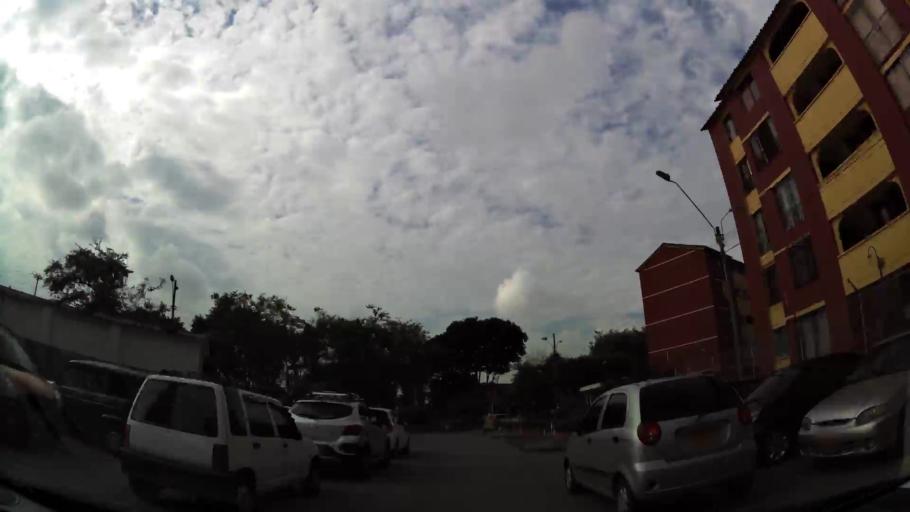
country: CO
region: Valle del Cauca
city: Cali
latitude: 3.4758
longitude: -76.4910
